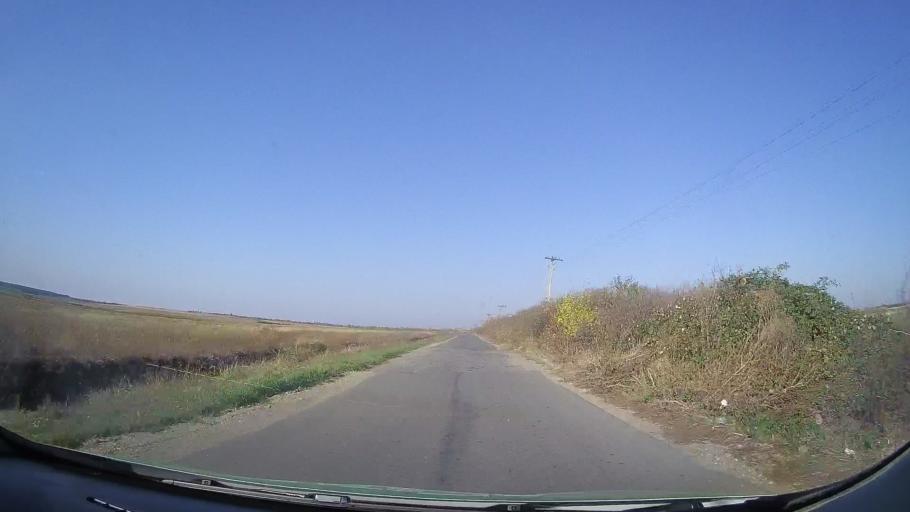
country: RO
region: Satu Mare
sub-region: Oras Tasnad
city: Tasnad
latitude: 47.4778
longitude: 22.5519
